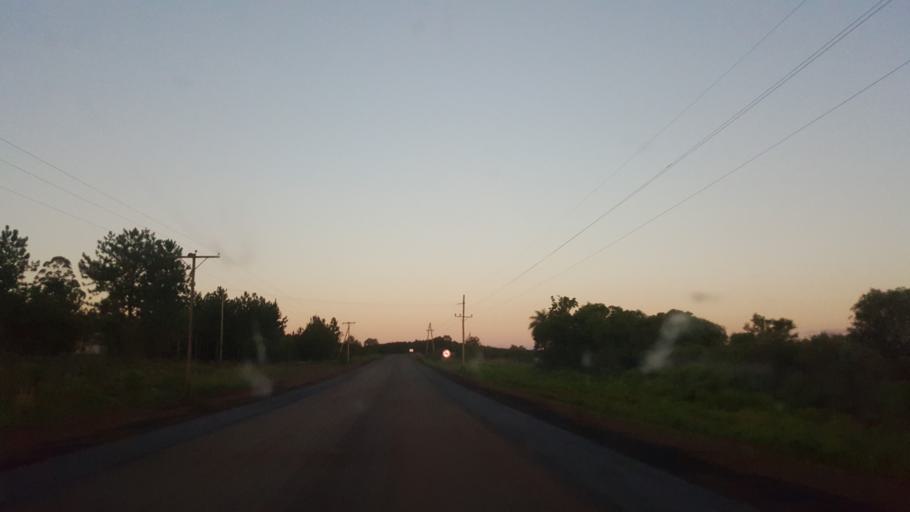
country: AR
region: Corrientes
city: Garruchos
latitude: -28.2307
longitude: -55.8089
